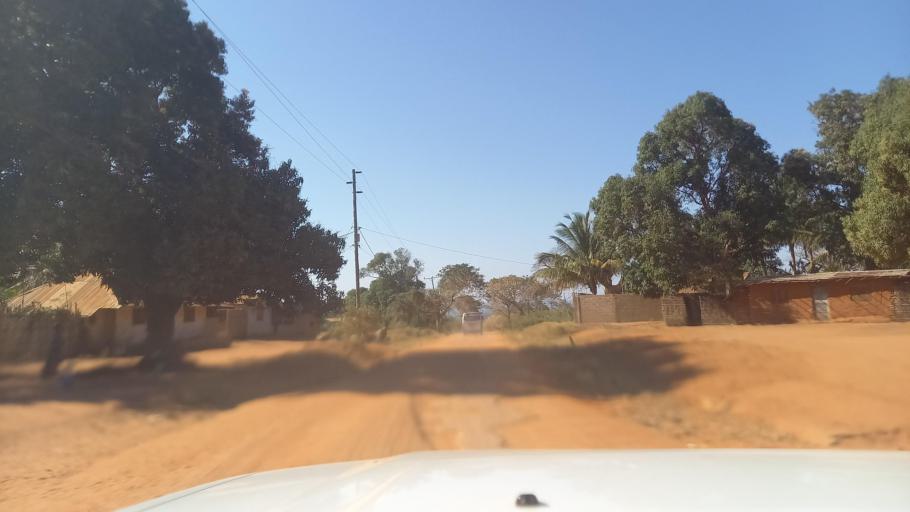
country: MZ
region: Cabo Delgado
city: Pemba
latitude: -13.0914
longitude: 40.5305
